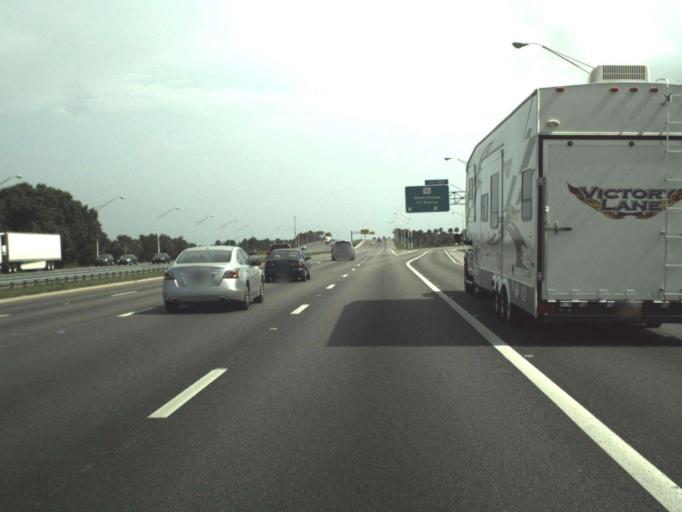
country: US
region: Florida
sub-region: Saint Lucie County
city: Fort Pierce South
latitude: 27.4235
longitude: -80.3886
